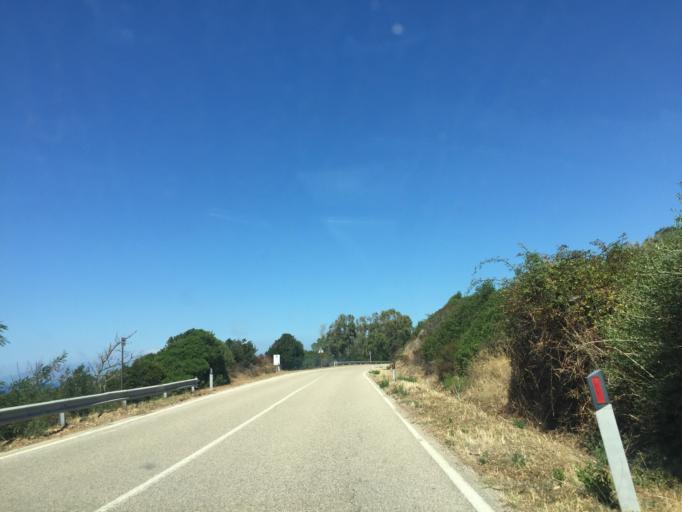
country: IT
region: Sardinia
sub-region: Provincia di Olbia-Tempio
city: Aglientu
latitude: 41.1008
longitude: 9.0833
